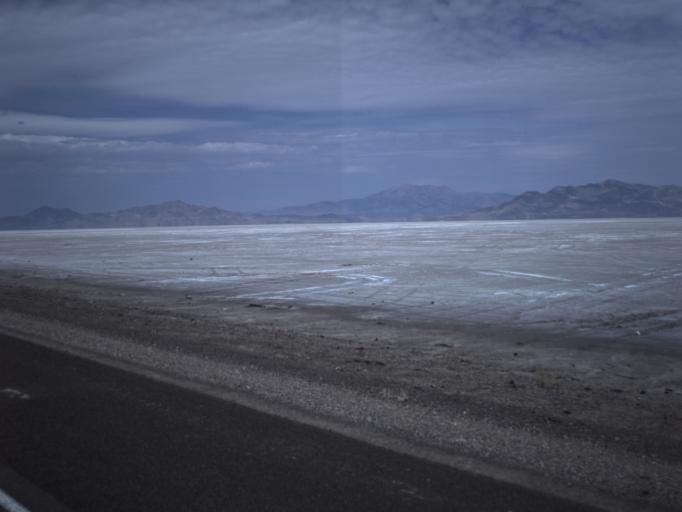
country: US
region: Utah
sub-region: Tooele County
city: Wendover
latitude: 40.7357
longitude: -113.6720
